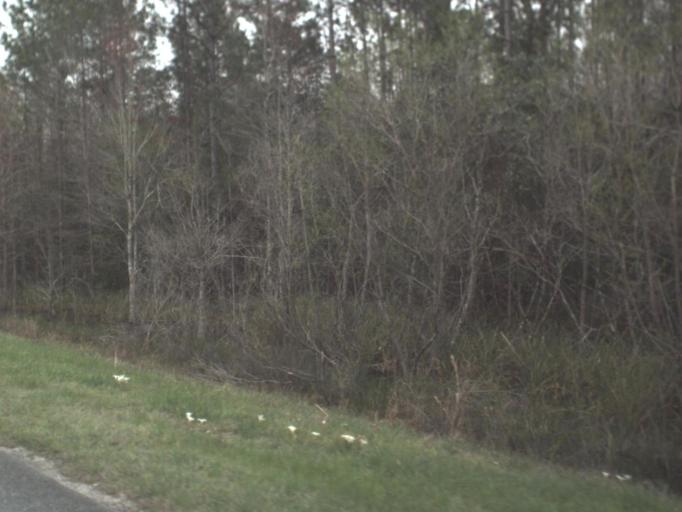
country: US
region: Florida
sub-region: Leon County
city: Woodville
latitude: 30.1950
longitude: -84.1376
